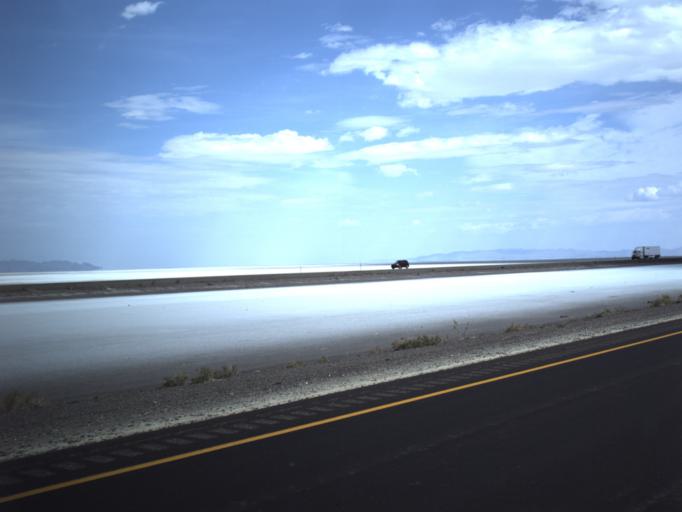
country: US
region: Utah
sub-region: Tooele County
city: Wendover
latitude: 40.7341
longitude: -113.6401
